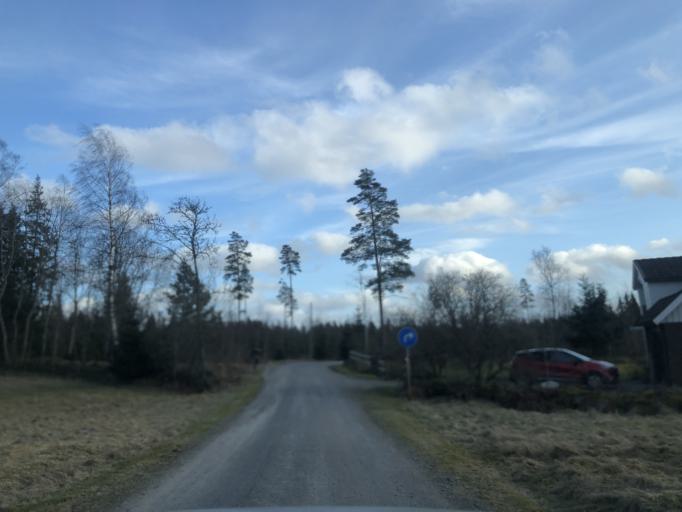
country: SE
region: Vaestra Goetaland
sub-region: Ulricehamns Kommun
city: Ulricehamn
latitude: 57.7766
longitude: 13.4362
